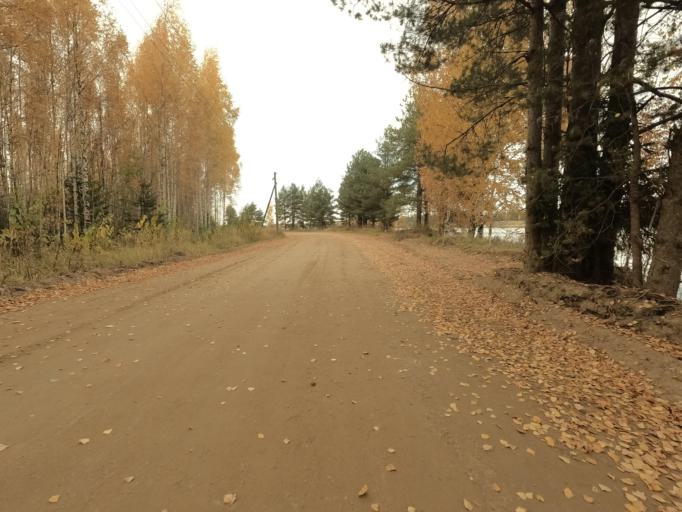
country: RU
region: Leningrad
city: Priladozhskiy
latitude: 59.7123
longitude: 31.3534
